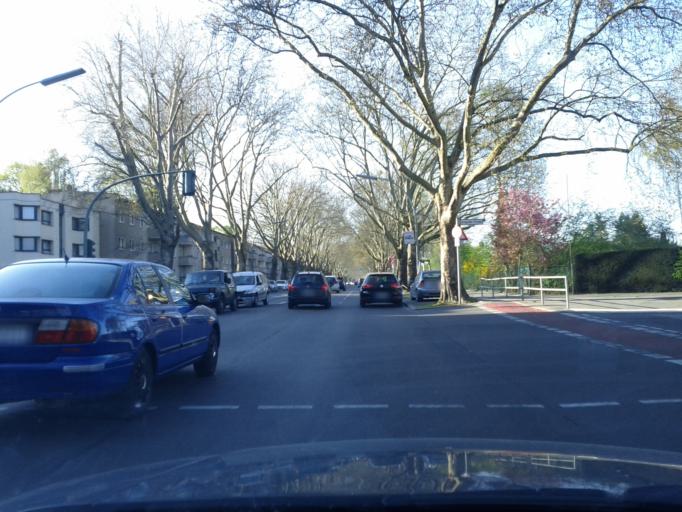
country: DE
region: Berlin
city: Reinickendorf
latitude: 52.5813
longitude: 13.3452
